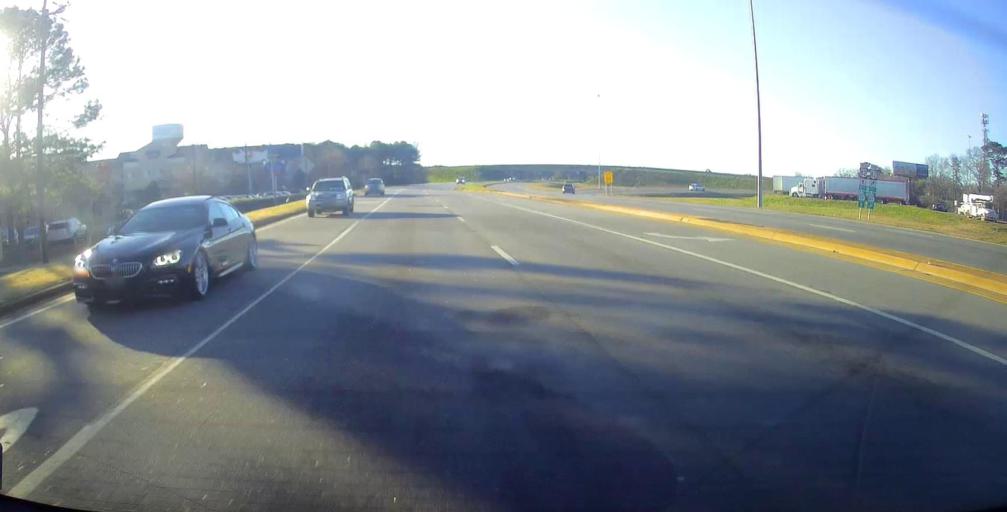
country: US
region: Georgia
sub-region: Dougherty County
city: Albany
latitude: 31.6207
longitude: -84.2271
